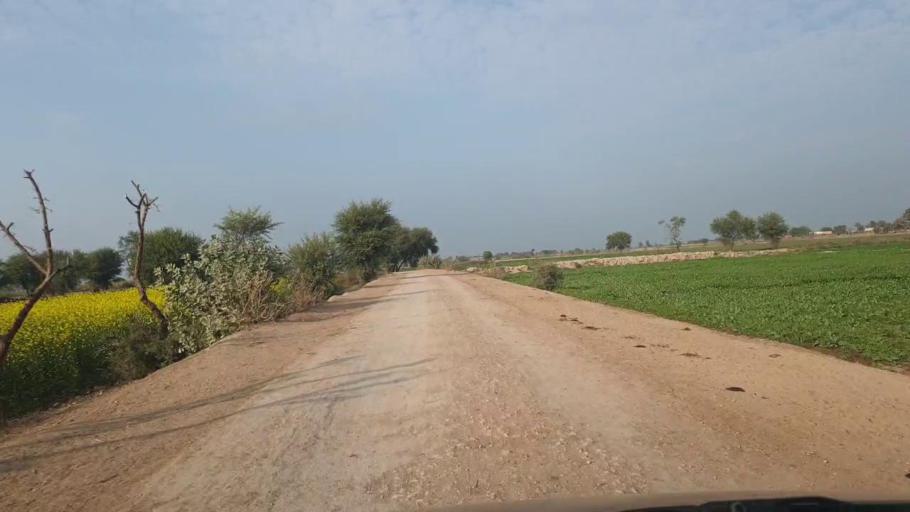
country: PK
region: Sindh
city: Shahdadpur
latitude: 25.8733
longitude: 68.7138
